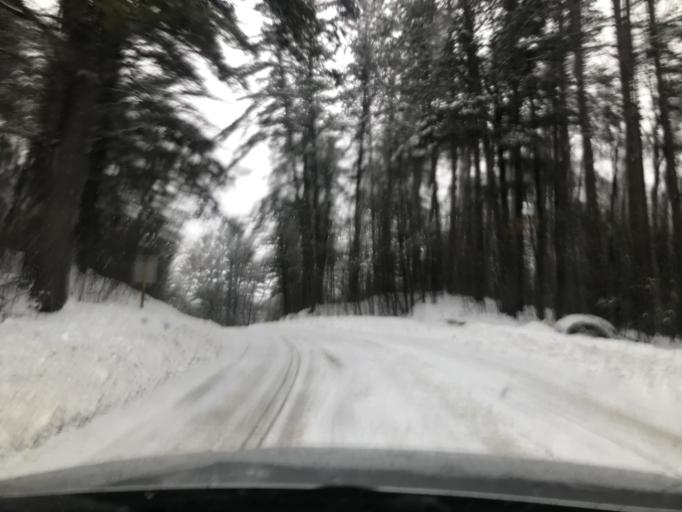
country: US
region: Wisconsin
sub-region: Marinette County
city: Peshtigo
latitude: 45.3808
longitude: -87.9505
